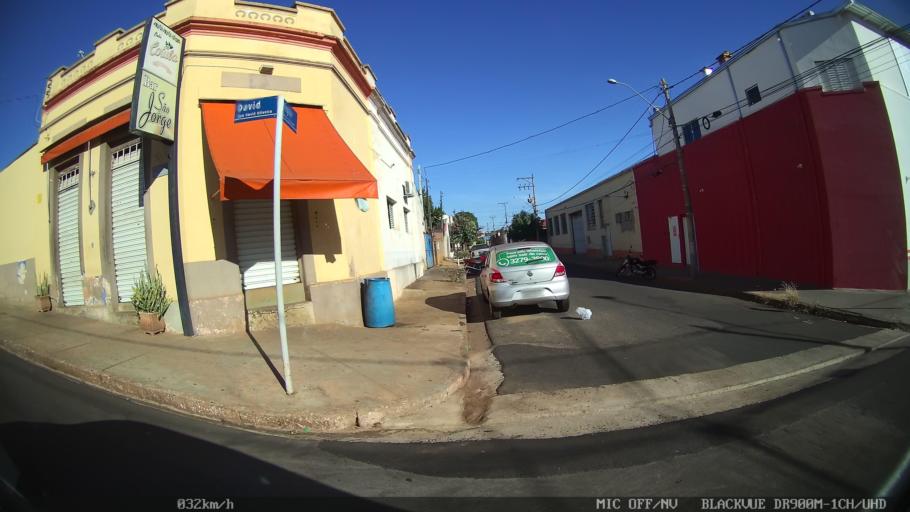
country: BR
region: Sao Paulo
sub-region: Olimpia
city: Olimpia
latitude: -20.7379
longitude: -48.9103
